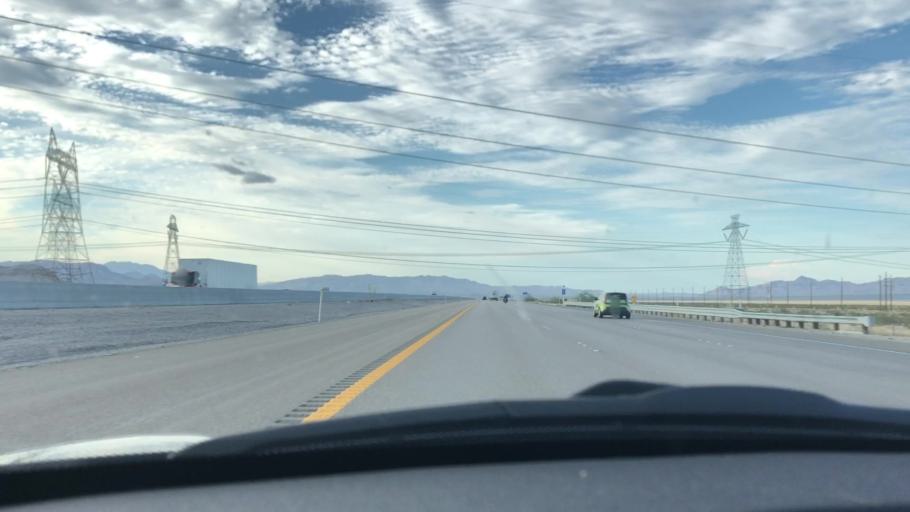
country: US
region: Nevada
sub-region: Clark County
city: Sandy Valley
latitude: 35.6212
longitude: -115.3866
